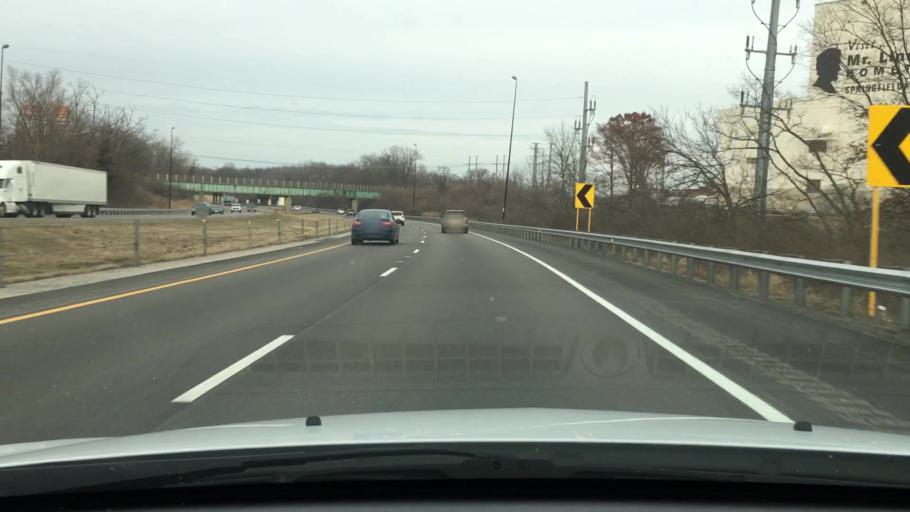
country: US
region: Illinois
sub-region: Sangamon County
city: Southern View
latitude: 39.7548
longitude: -89.6076
